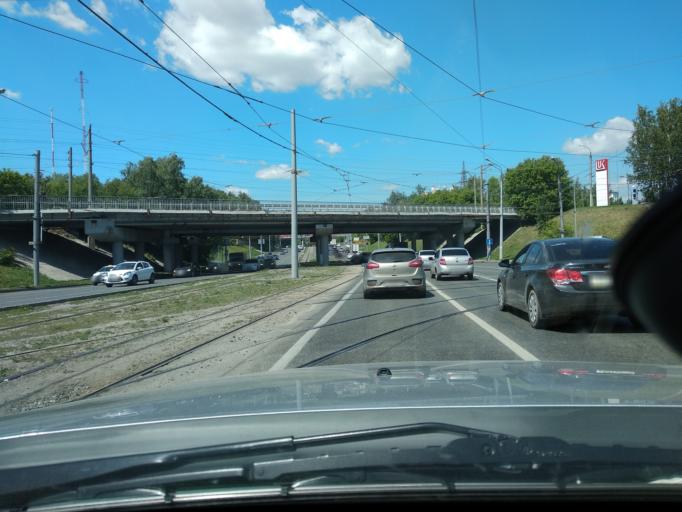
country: RU
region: Tatarstan
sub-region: Gorod Kazan'
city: Kazan
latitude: 55.8163
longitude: 49.1805
